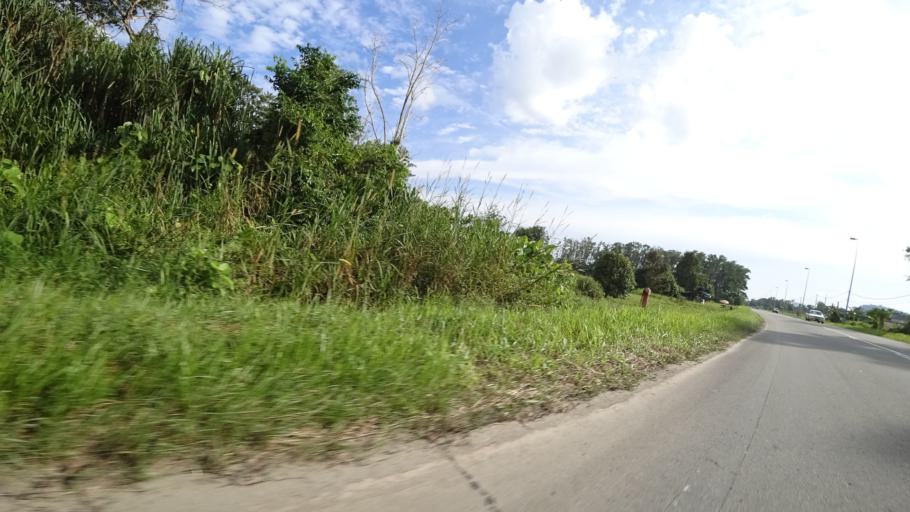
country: MY
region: Sarawak
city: Limbang
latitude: 4.7952
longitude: 114.8442
